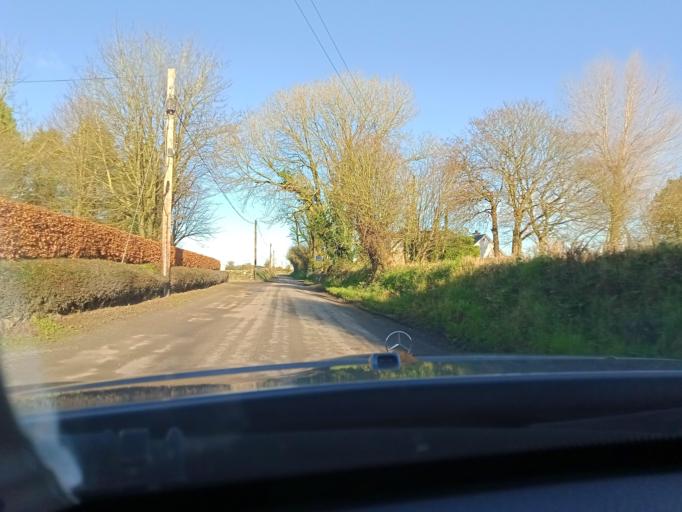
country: IE
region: Leinster
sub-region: Kilkenny
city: Mooncoin
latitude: 52.2856
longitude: -7.2356
